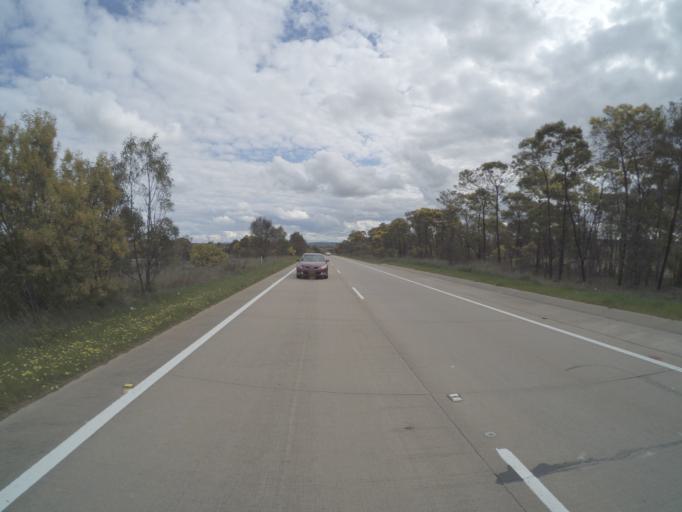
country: AU
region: New South Wales
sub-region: Goulburn Mulwaree
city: Goulburn
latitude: -34.8083
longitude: 149.4867
